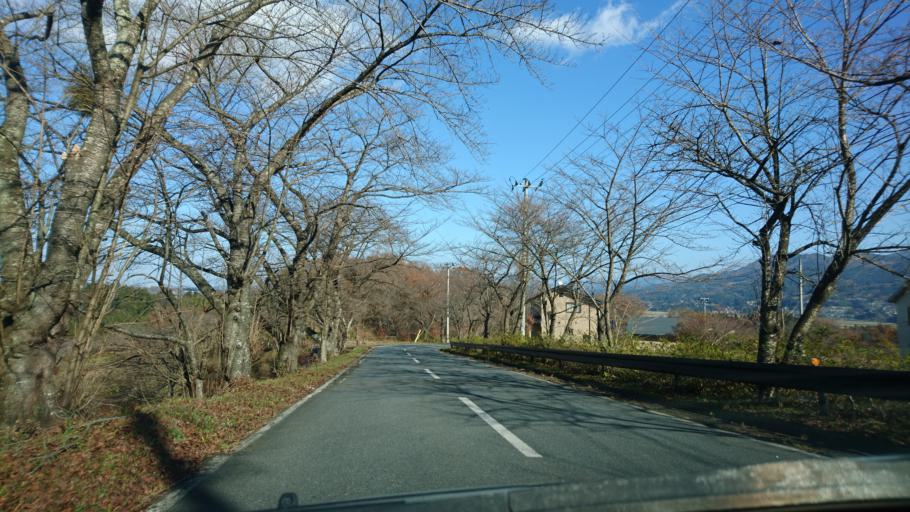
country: JP
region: Iwate
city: Ichinoseki
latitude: 38.9938
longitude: 141.1043
